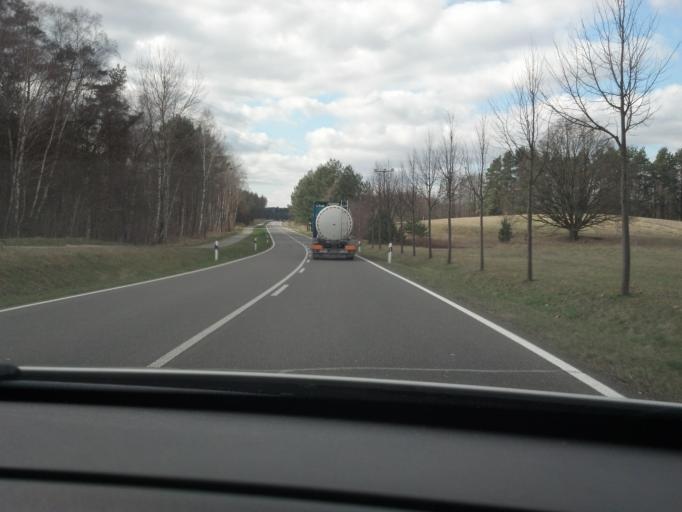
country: DE
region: Mecklenburg-Vorpommern
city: Neustrelitz
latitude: 53.3014
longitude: 13.0654
